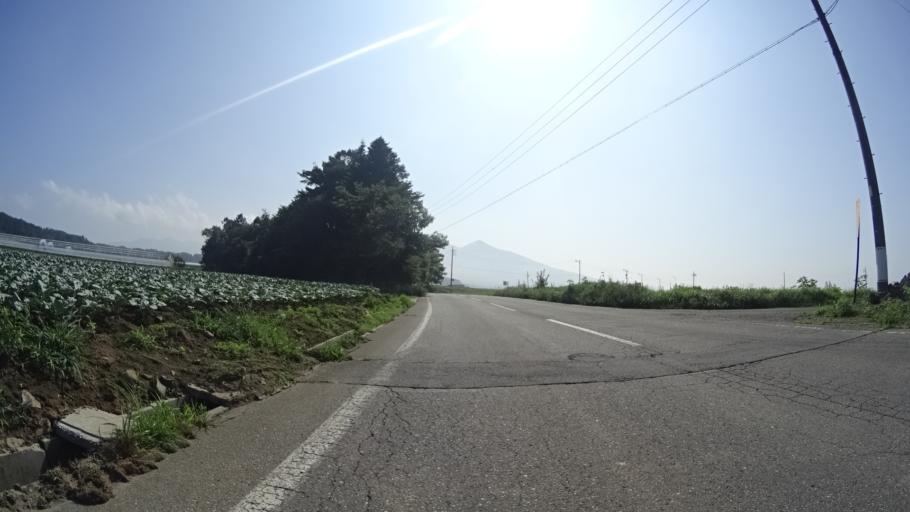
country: JP
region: Nagano
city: Chino
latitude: 35.9439
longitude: 138.2464
